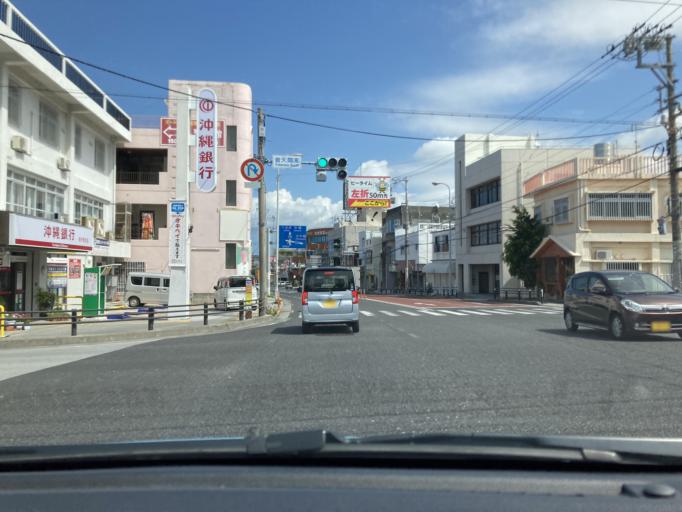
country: JP
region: Okinawa
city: Chatan
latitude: 26.2877
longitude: 127.7775
